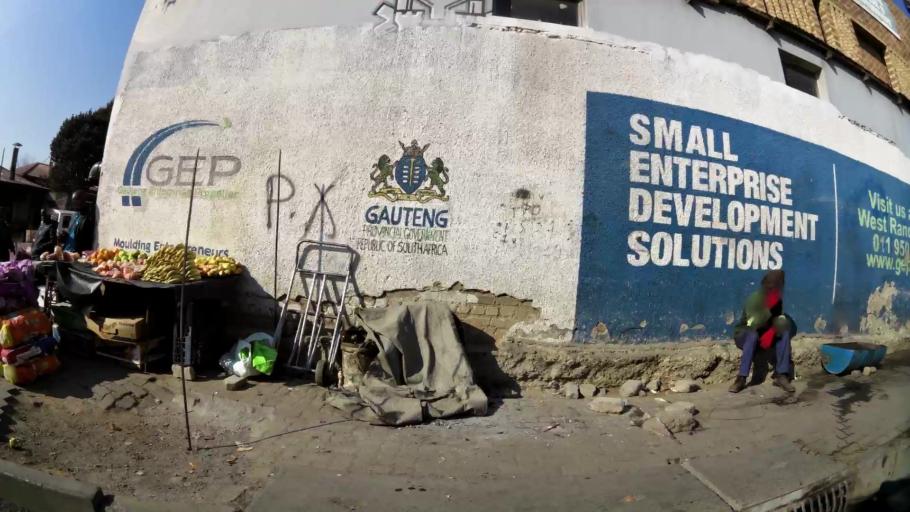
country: ZA
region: Gauteng
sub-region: City of Johannesburg Metropolitan Municipality
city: Modderfontein
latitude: -26.1068
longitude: 28.1043
